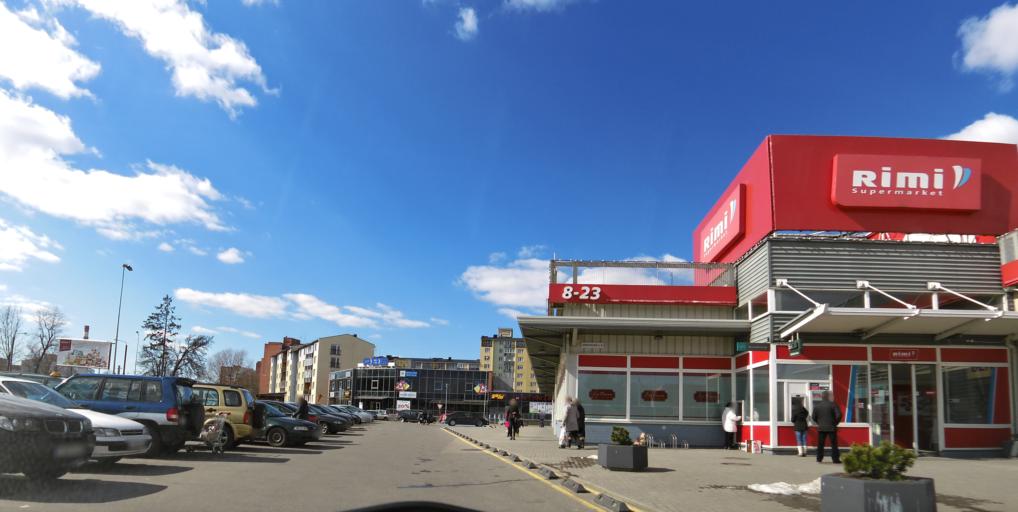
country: LT
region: Vilnius County
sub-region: Vilnius
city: Fabijoniskes
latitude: 54.7398
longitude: 25.2750
